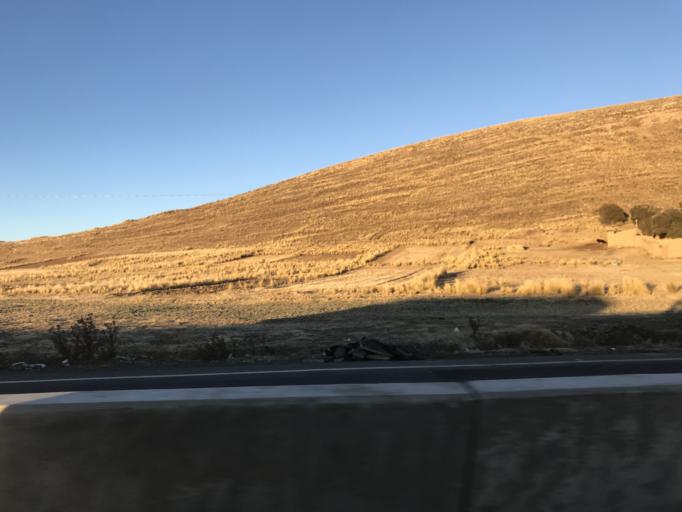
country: BO
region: La Paz
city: Batallas
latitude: -16.3025
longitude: -68.4835
